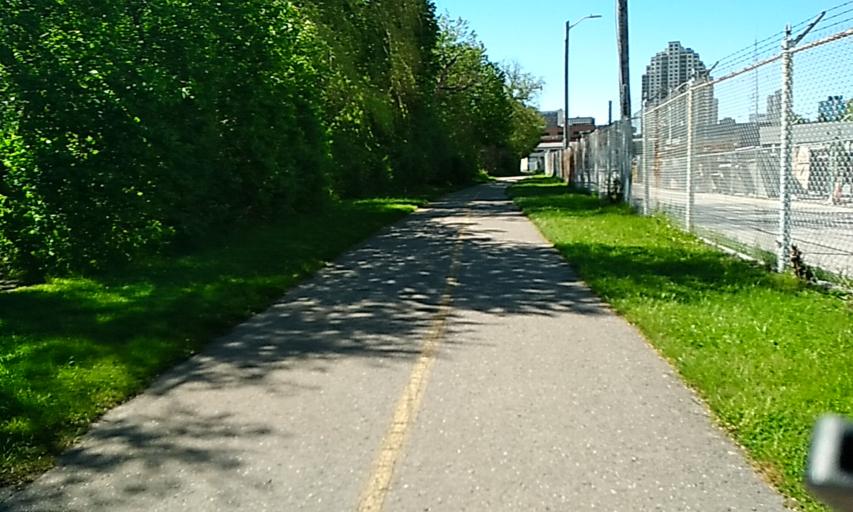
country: CA
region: Ontario
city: London
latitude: 42.9753
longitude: -81.2490
